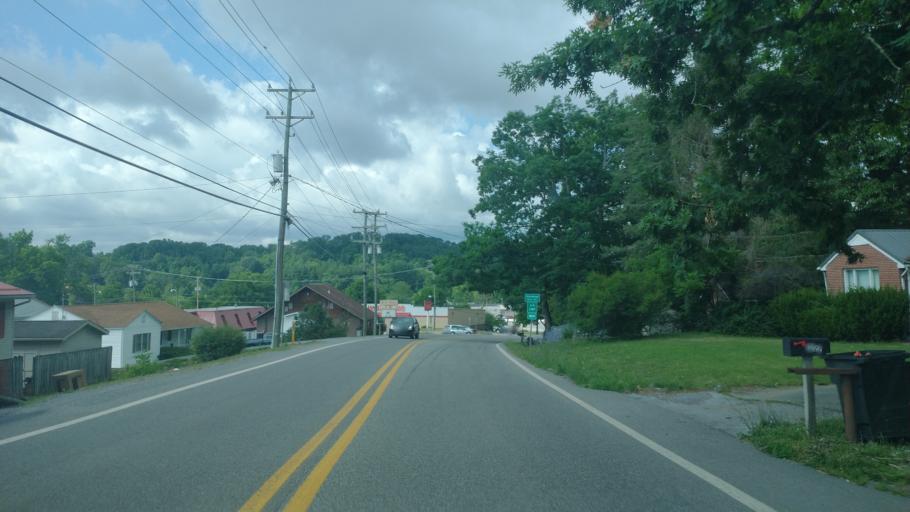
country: US
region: West Virginia
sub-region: Mercer County
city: Princeton
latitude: 37.3460
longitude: -81.1557
